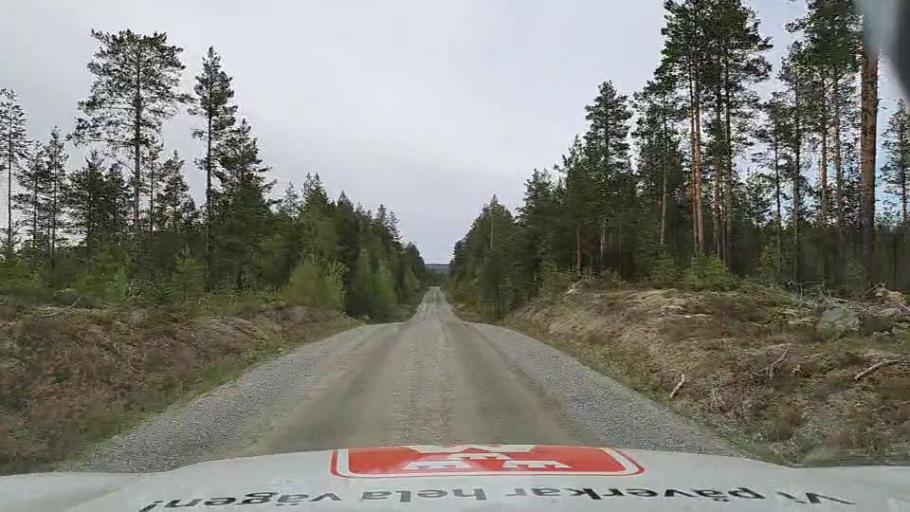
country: SE
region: Jaemtland
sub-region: Braecke Kommun
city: Braecke
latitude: 62.4762
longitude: 14.9167
